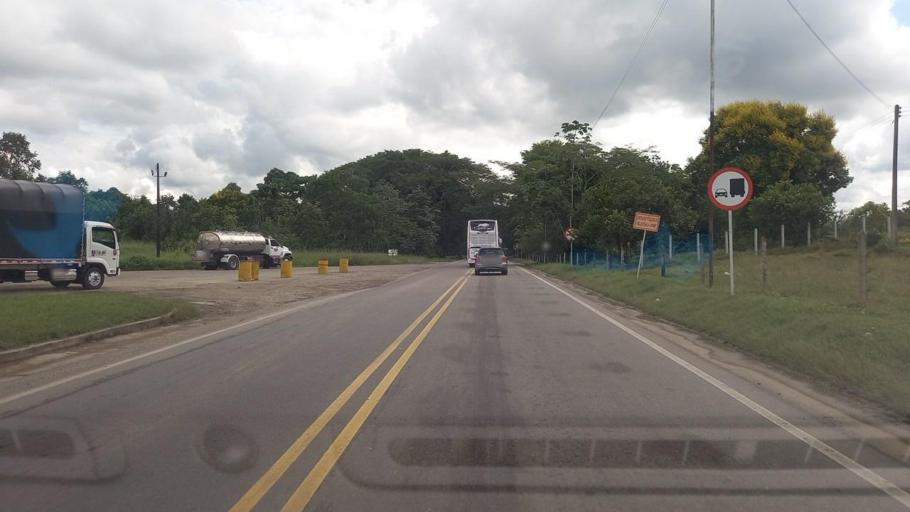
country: CO
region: Santander
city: Barrancabermeja
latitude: 7.1235
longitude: -73.5872
